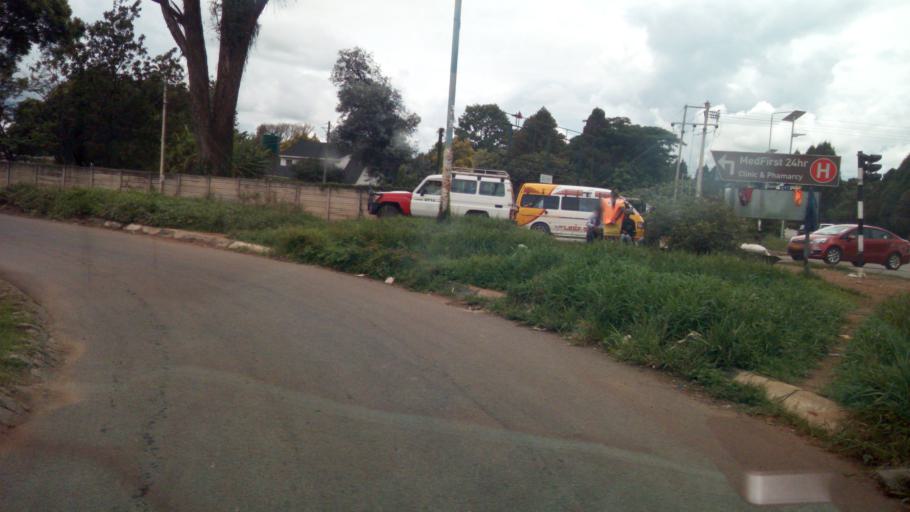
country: ZW
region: Harare
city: Harare
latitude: -17.7517
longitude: 31.0282
